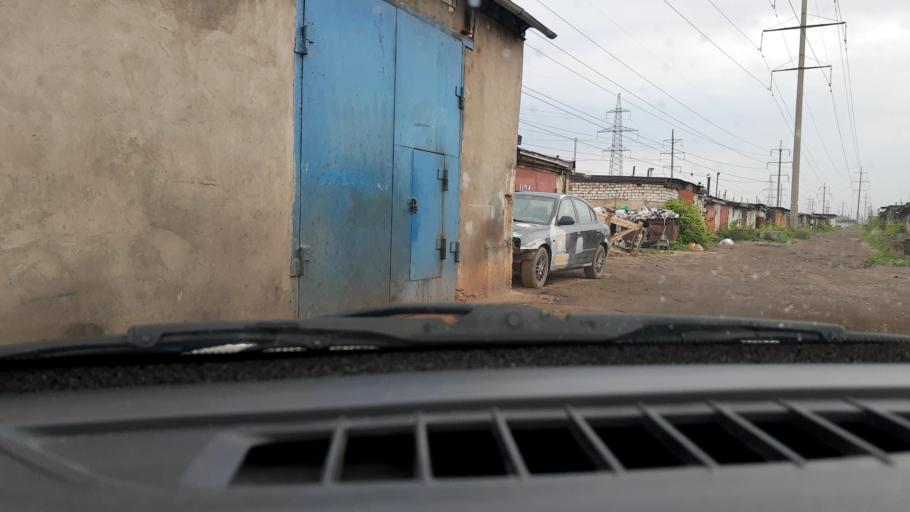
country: RU
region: Nizjnij Novgorod
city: Nizhniy Novgorod
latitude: 56.2700
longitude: 43.9009
